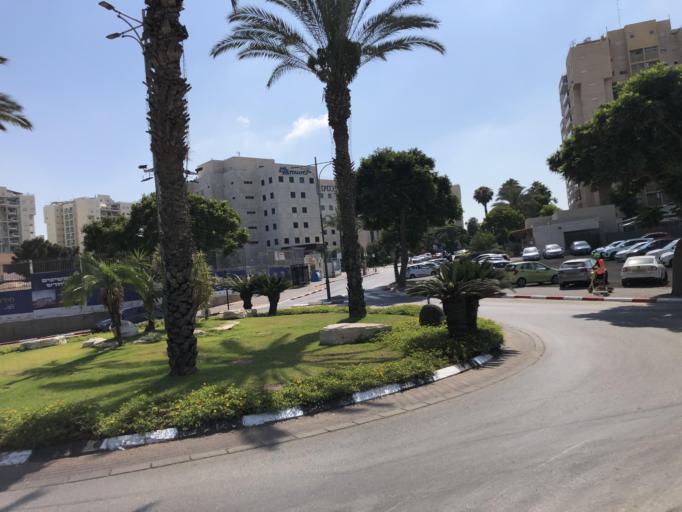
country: IL
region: Central District
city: Yehud
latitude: 32.0326
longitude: 34.8774
